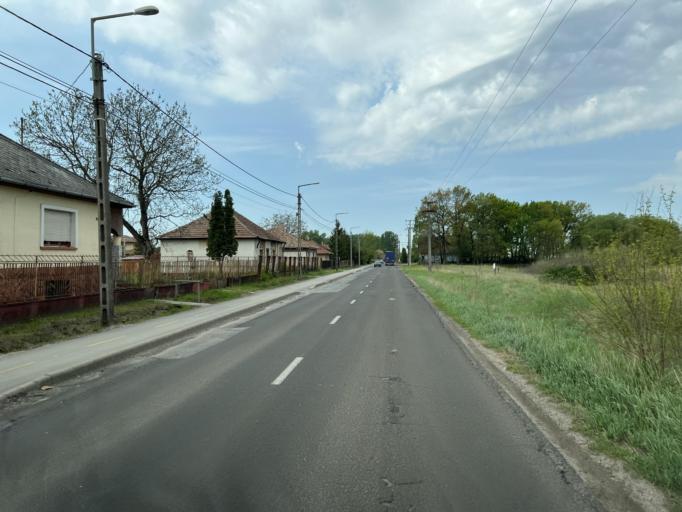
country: HU
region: Pest
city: Farmos
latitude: 47.3687
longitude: 19.8596
